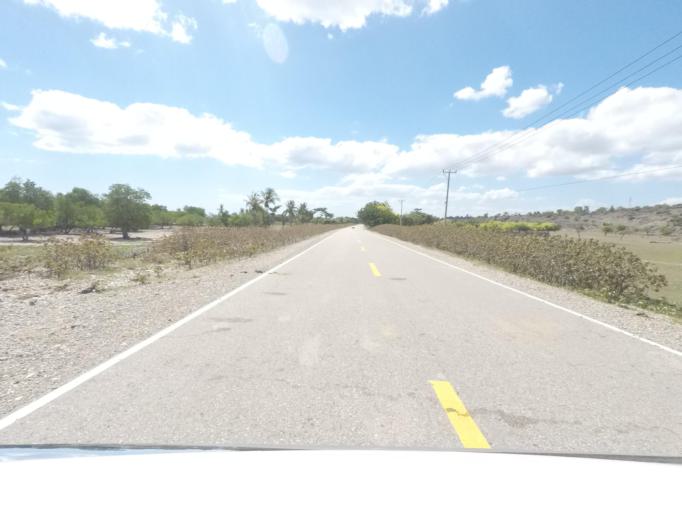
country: TL
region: Baucau
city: Baucau
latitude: -8.4369
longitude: 126.6672
